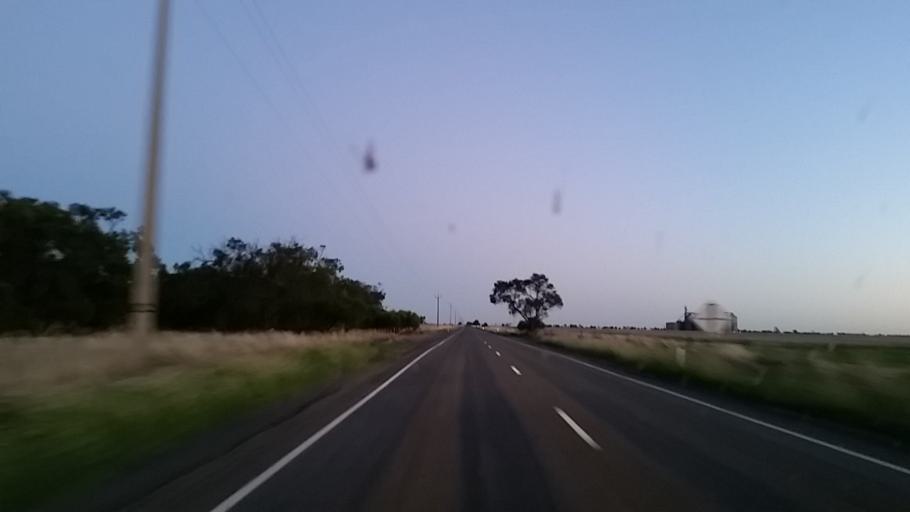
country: AU
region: South Australia
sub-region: Wakefield
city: Balaklava
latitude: -34.1680
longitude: 138.4297
